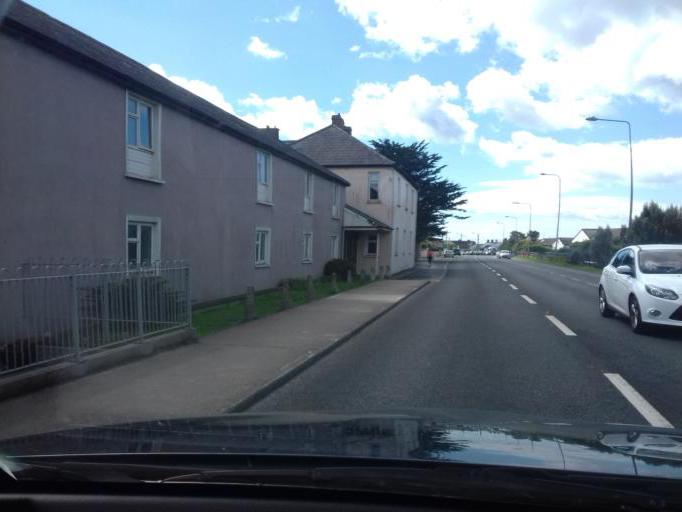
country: IE
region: Munster
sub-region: Waterford
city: Tra Mhor
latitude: 52.1639
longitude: -7.1394
